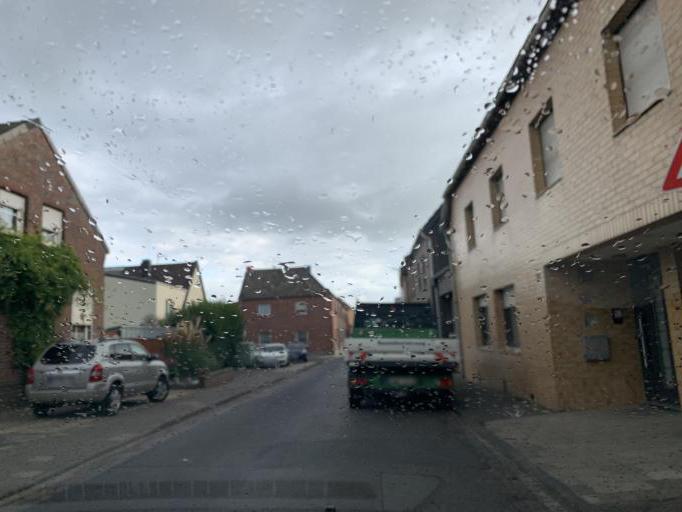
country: DE
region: North Rhine-Westphalia
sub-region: Regierungsbezirk Koln
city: Linnich
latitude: 50.9656
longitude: 6.2744
